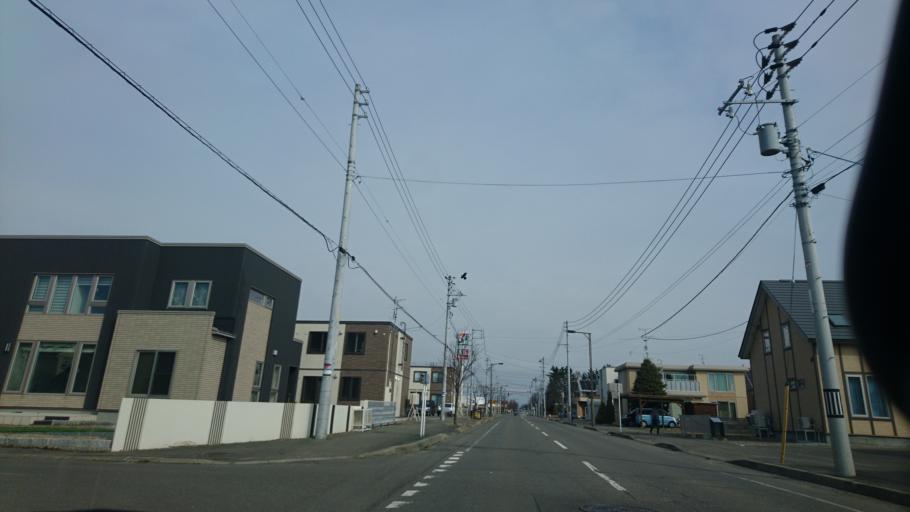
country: JP
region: Hokkaido
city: Otofuke
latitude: 42.9714
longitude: 143.2125
